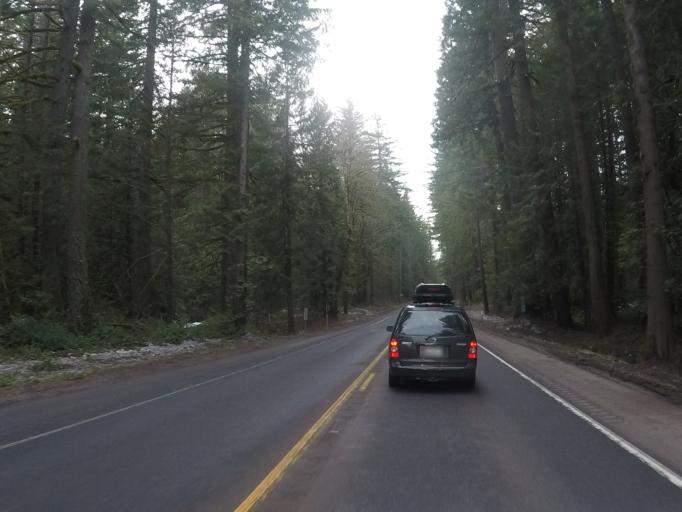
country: US
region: Oregon
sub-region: Clackamas County
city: Mount Hood Village
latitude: 45.3150
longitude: -121.8974
